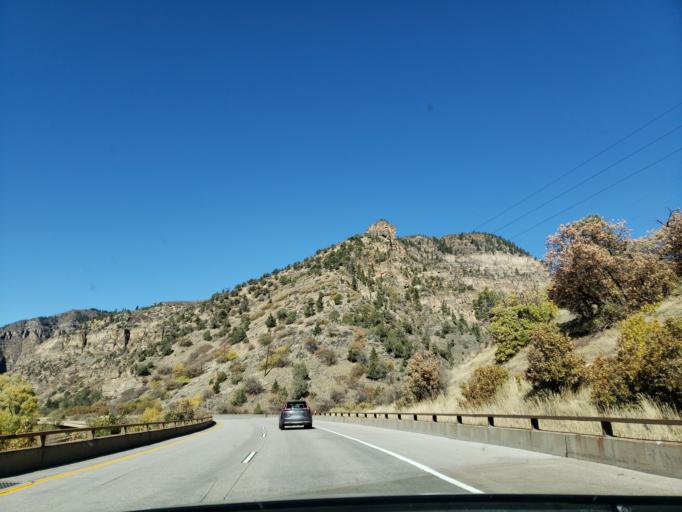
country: US
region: Colorado
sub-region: Garfield County
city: Glenwood Springs
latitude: 39.5603
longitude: -107.2486
